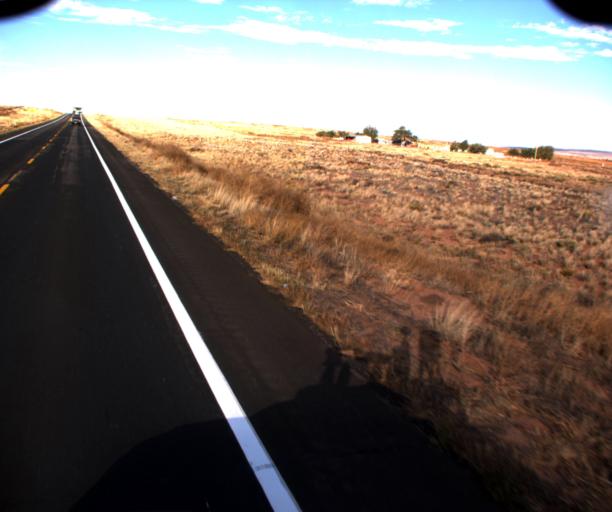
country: US
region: Arizona
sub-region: Apache County
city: Lukachukai
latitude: 36.9613
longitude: -109.3970
